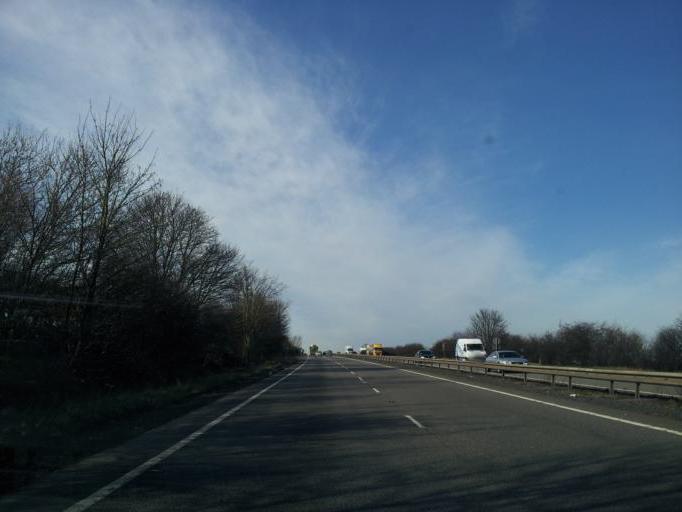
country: GB
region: England
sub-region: Lincolnshire
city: Grantham
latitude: 52.8849
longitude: -0.6403
